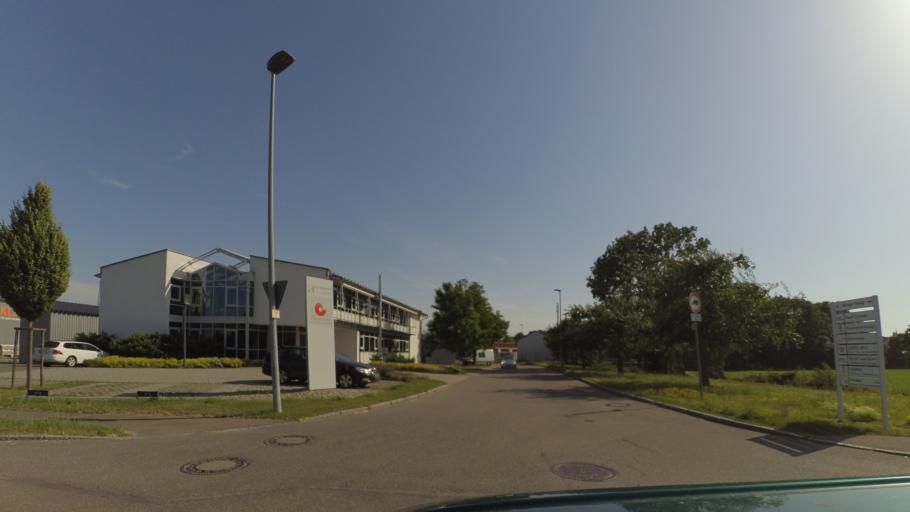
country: DE
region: Baden-Wuerttemberg
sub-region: Regierungsbezirk Stuttgart
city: Hermaringen
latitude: 48.5940
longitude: 10.2671
